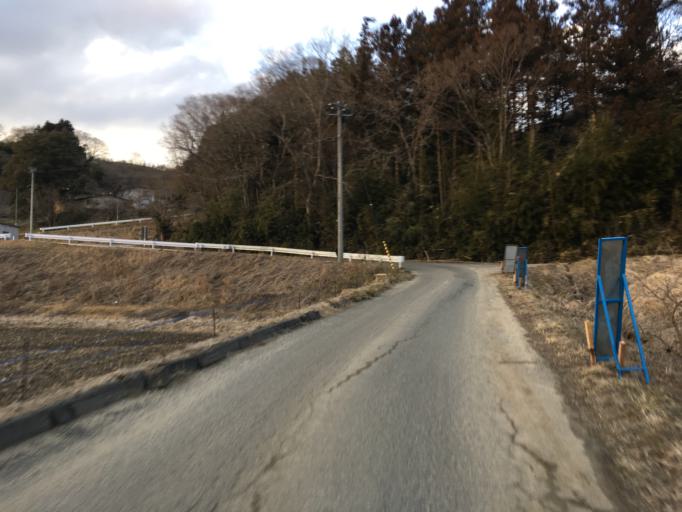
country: JP
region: Fukushima
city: Fukushima-shi
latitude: 37.6550
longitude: 140.5505
